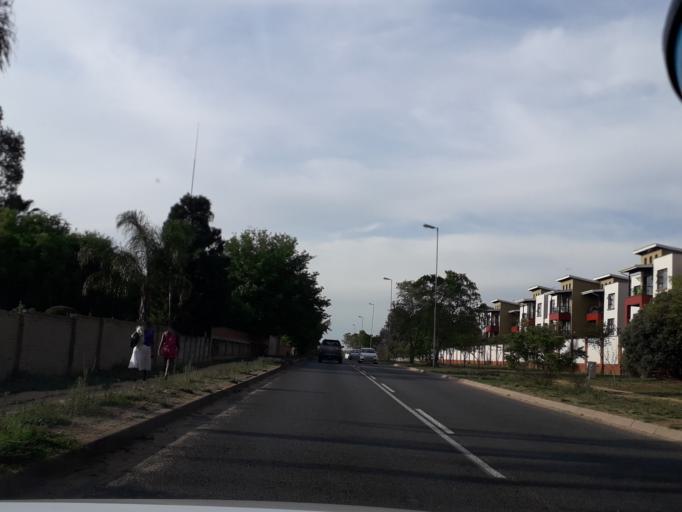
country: ZA
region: Gauteng
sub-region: City of Johannesburg Metropolitan Municipality
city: Diepsloot
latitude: -26.0332
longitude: 27.9923
